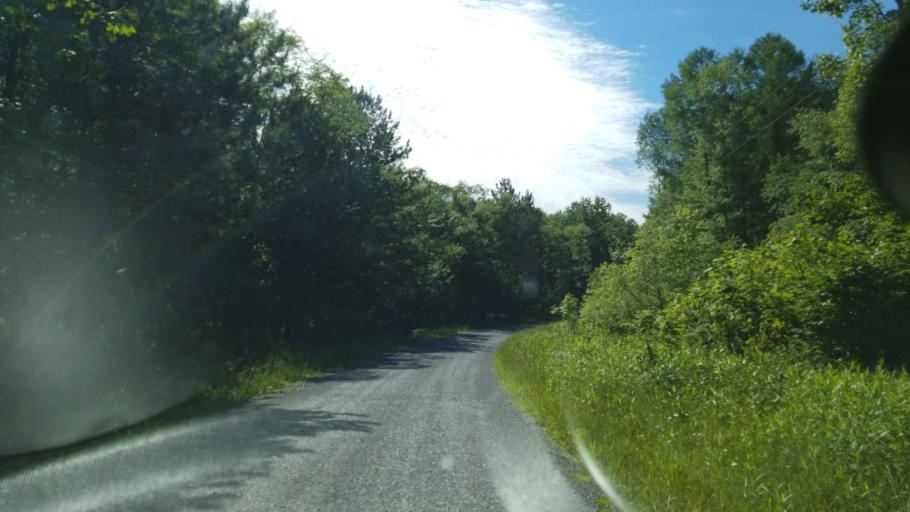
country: US
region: Pennsylvania
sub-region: Clearfield County
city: Clearfield
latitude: 41.1892
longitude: -78.4677
